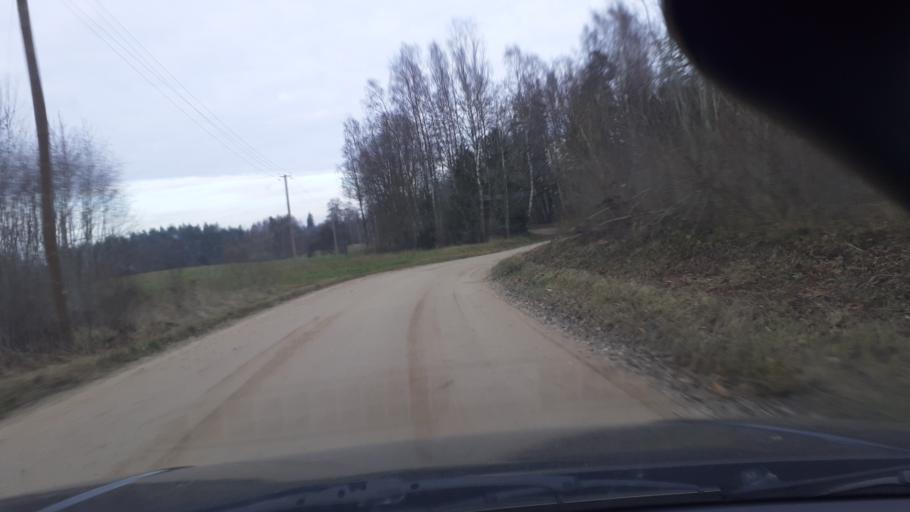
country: LV
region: Alsunga
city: Alsunga
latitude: 56.9758
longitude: 21.6668
